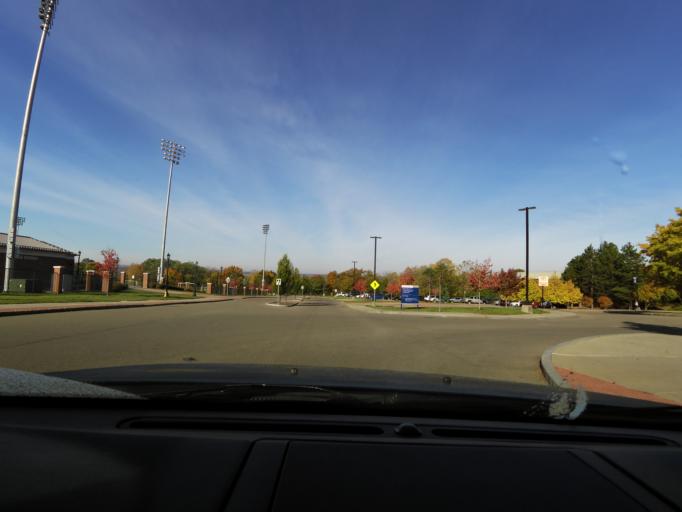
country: US
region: New York
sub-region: Livingston County
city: Geneseo
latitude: 42.7957
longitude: -77.8246
